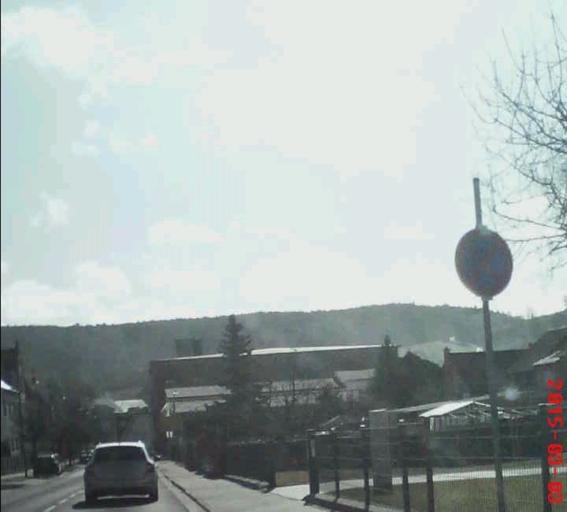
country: DE
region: Thuringia
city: Stadtilm
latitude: 50.7782
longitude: 11.0805
